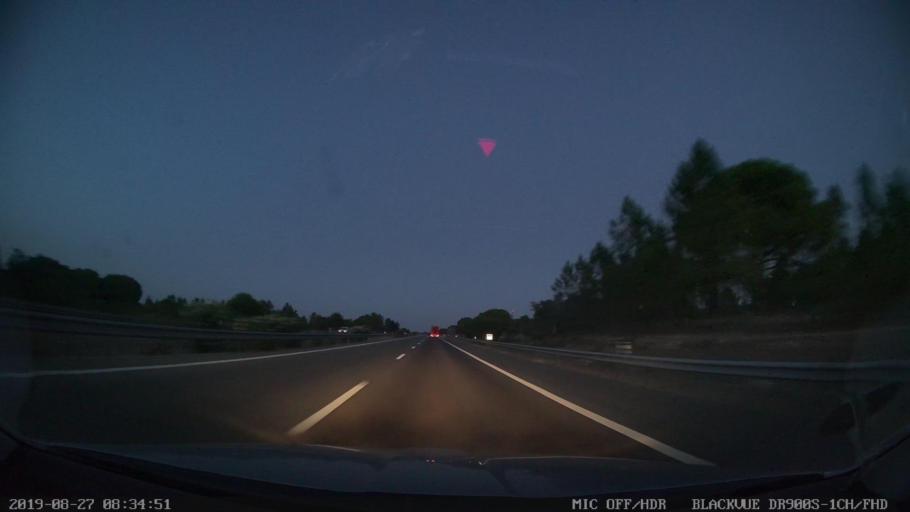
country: PT
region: Evora
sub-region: Vendas Novas
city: Vendas Novas
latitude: 38.6332
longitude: -8.5311
